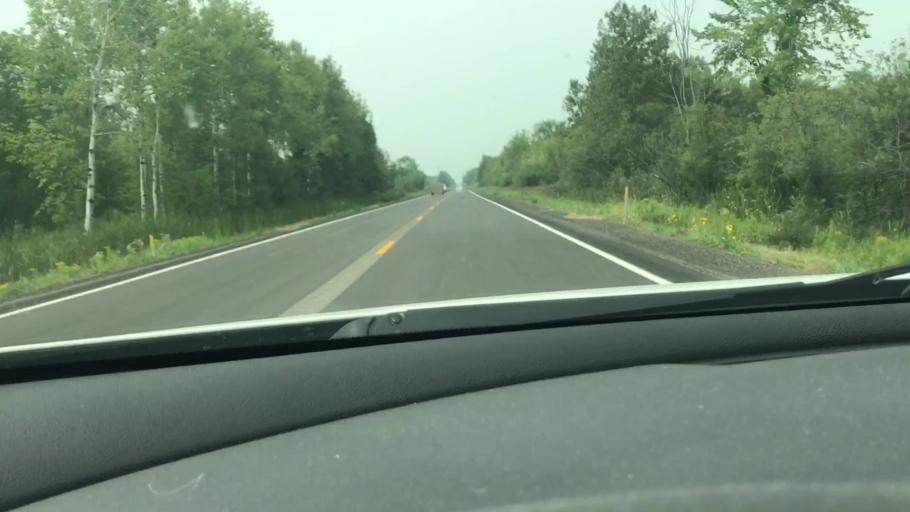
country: US
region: Minnesota
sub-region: Itasca County
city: Cohasset
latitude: 47.3616
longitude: -93.8656
